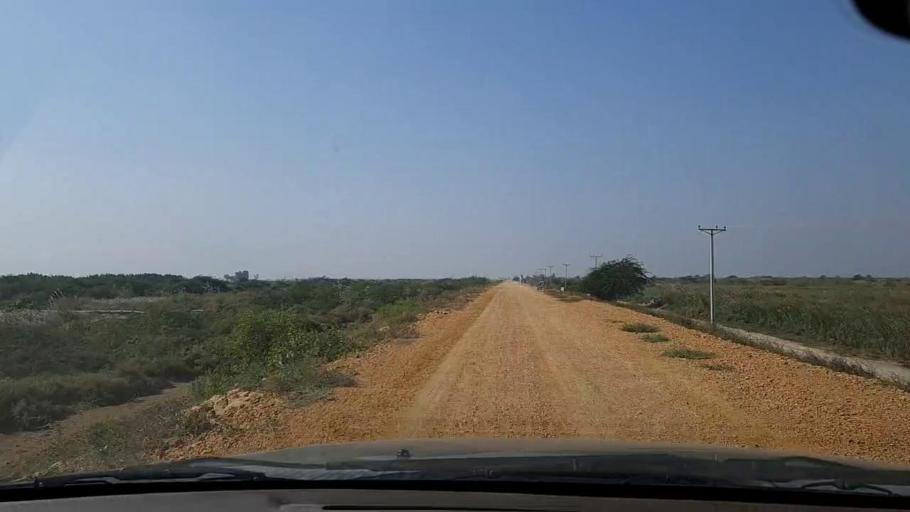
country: PK
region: Sindh
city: Chuhar Jamali
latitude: 24.4615
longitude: 67.8965
